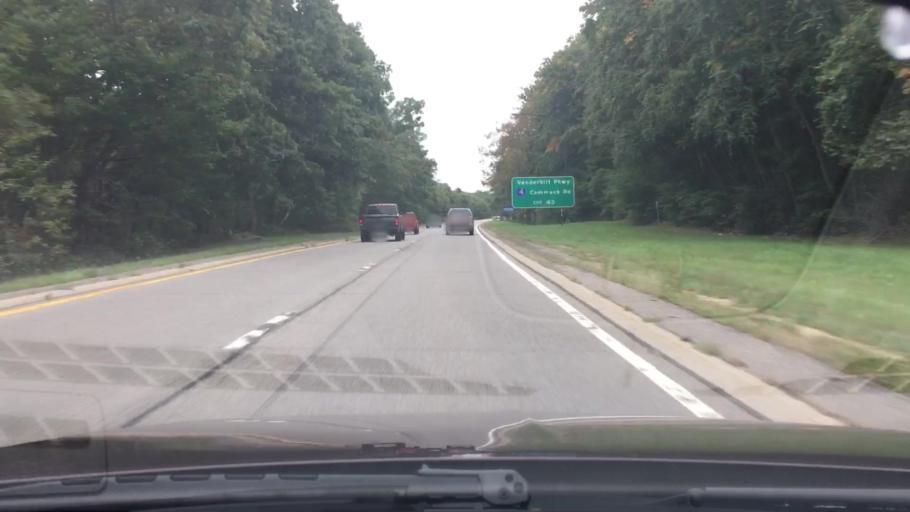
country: US
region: New York
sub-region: Suffolk County
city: Elwood
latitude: 40.8276
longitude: -73.3208
